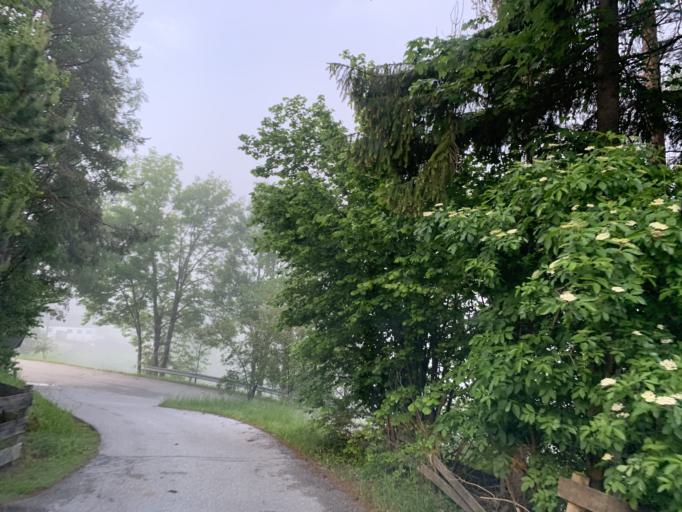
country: AT
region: Salzburg
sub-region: Politischer Bezirk Sankt Johann im Pongau
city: Forstau
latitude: 47.3977
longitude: 13.5920
